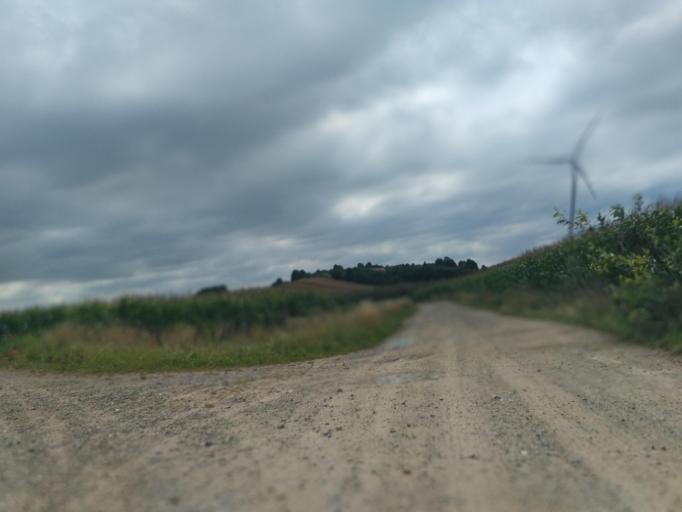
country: PL
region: Subcarpathian Voivodeship
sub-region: Powiat krosnienski
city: Rymanow
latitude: 49.6201
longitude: 21.8465
